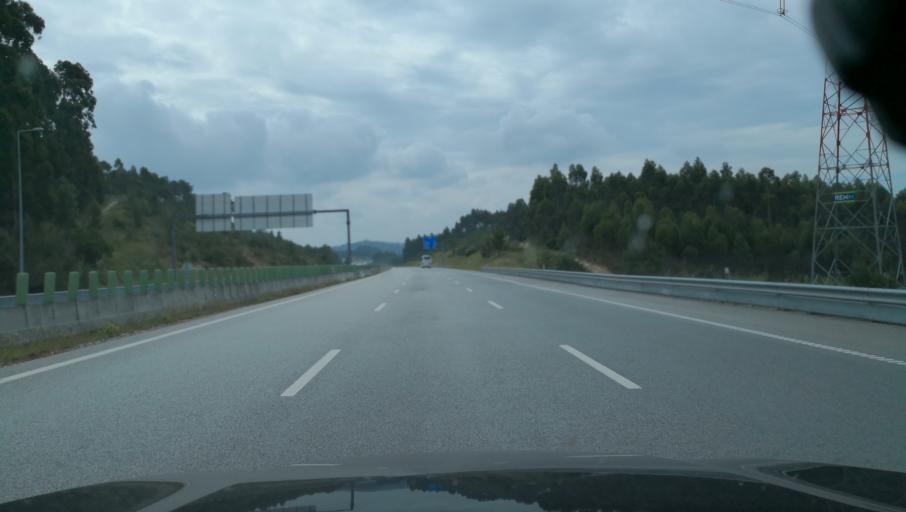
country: PT
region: Coimbra
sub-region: Figueira da Foz
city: Alhadas
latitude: 40.1557
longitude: -8.7721
